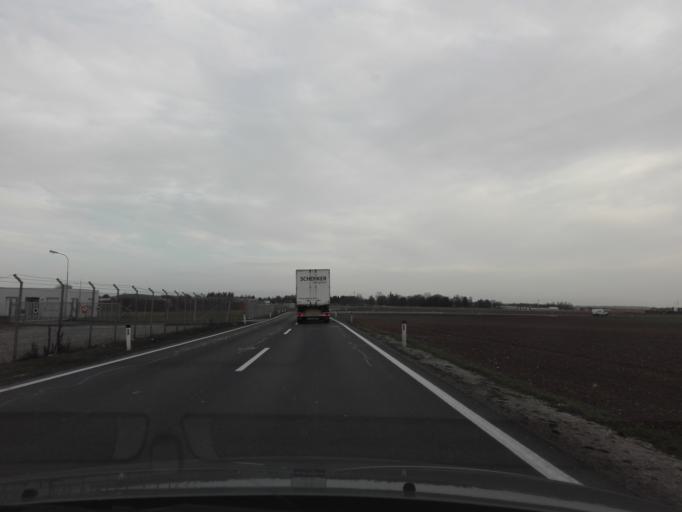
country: AT
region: Upper Austria
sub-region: Politischer Bezirk Linz-Land
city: Horsching
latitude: 48.2391
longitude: 14.1777
